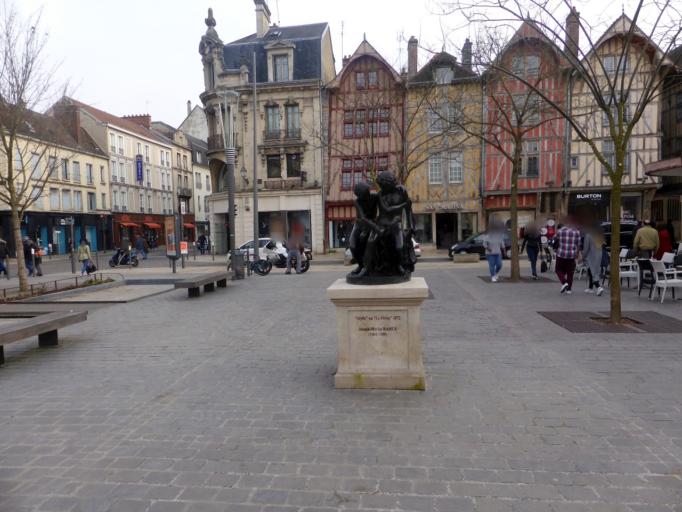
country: FR
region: Champagne-Ardenne
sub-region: Departement de l'Aube
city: Troyes
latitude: 48.2969
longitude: 4.0752
